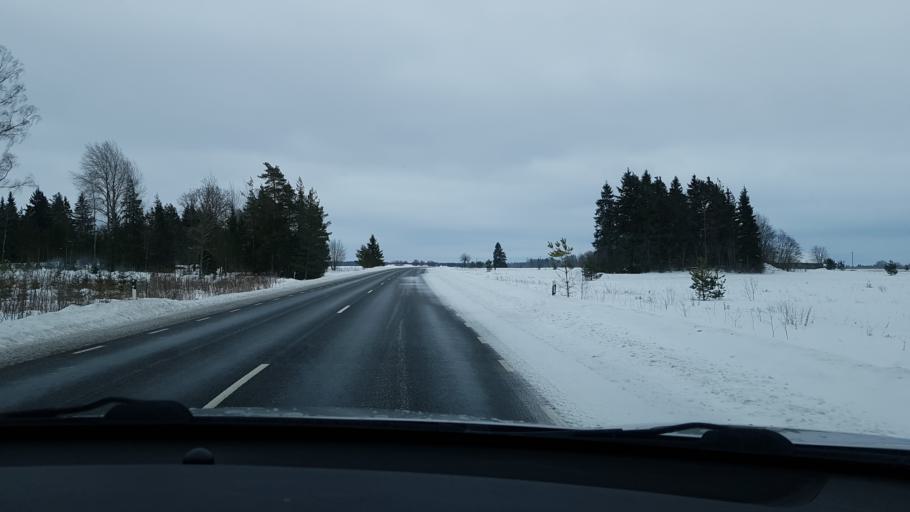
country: EE
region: Jaervamaa
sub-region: Jaerva-Jaani vald
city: Jarva-Jaani
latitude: 59.0919
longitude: 25.8294
